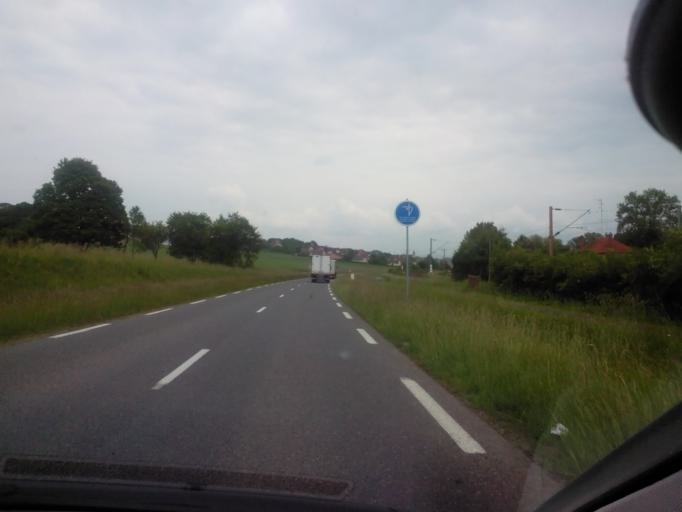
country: FR
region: Lorraine
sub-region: Departement de la Moselle
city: Sarrebourg
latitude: 48.7824
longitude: 7.0480
